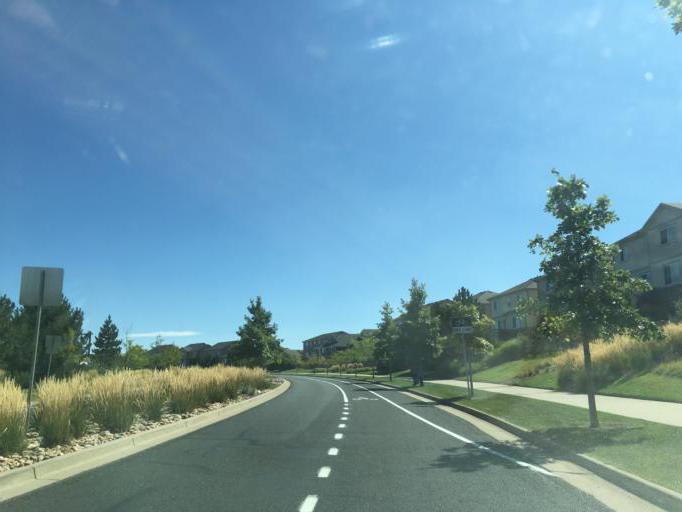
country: US
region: Colorado
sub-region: Douglas County
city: Parker
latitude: 39.5969
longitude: -104.6950
